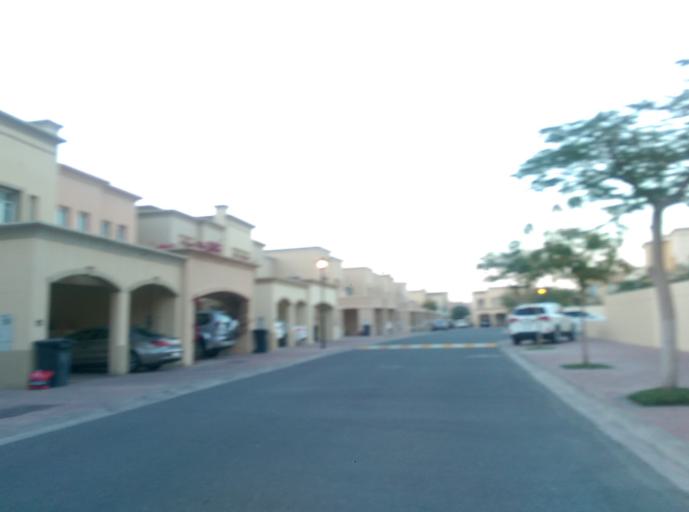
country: AE
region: Dubai
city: Dubai
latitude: 25.0515
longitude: 55.1742
